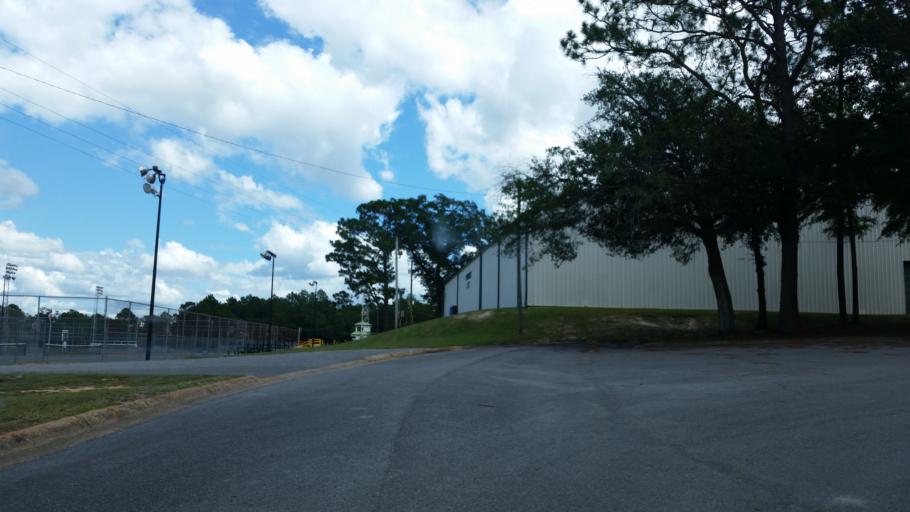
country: US
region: Florida
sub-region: Okaloosa County
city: Crestview
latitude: 30.7602
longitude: -86.5664
